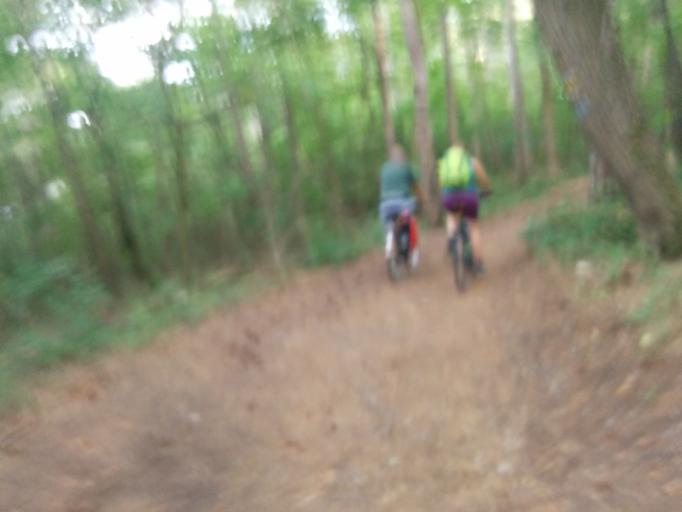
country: AT
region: Lower Austria
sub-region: Politischer Bezirk Modling
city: Gumpoldskirchen
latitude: 48.0530
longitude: 16.2667
